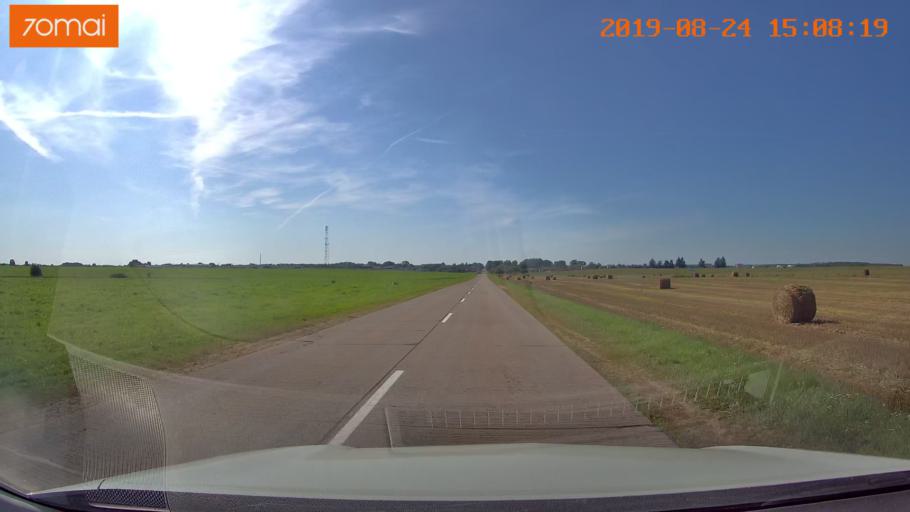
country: BY
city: Michanovichi
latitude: 53.6082
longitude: 27.6589
